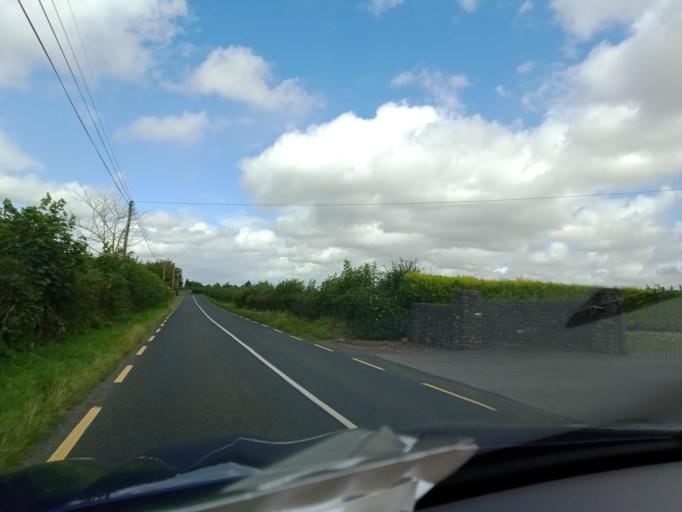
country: IE
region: Leinster
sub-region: Laois
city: Portlaoise
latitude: 53.0007
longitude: -7.2786
